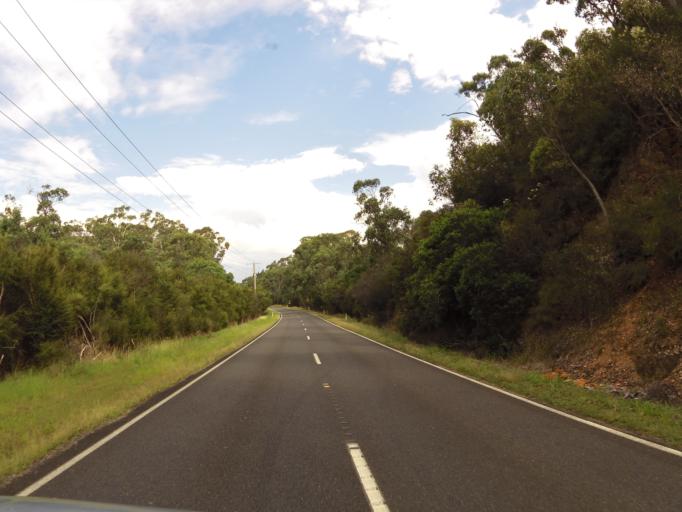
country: AU
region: Victoria
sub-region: Alpine
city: Mount Beauty
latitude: -36.7526
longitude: 147.0182
